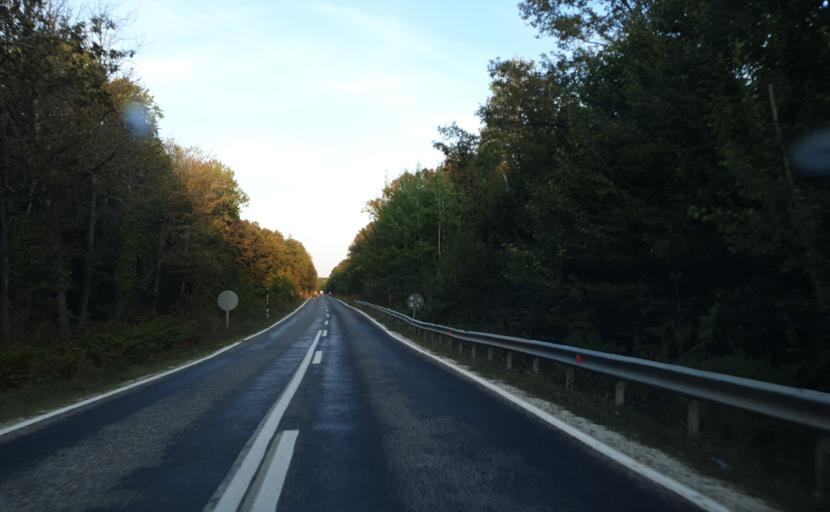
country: TR
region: Kirklareli
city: Igneada
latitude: 41.8758
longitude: 27.8197
